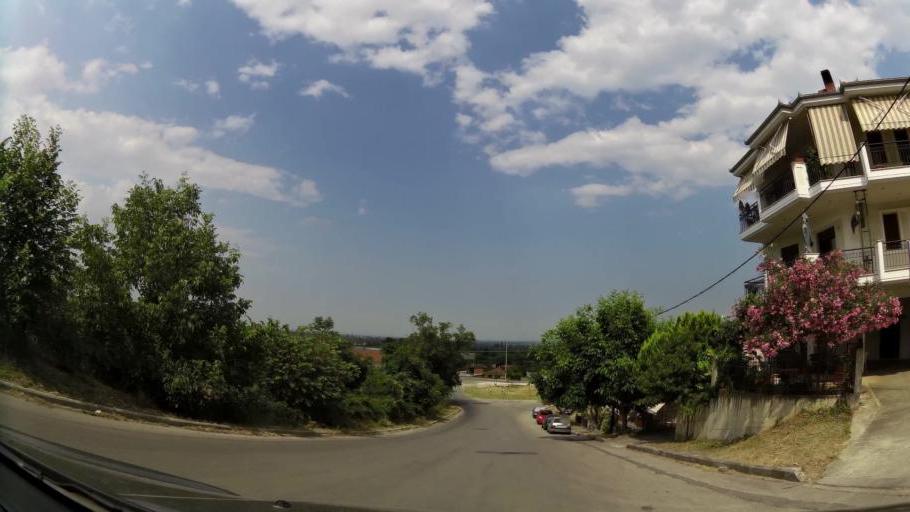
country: GR
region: Central Macedonia
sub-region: Nomos Imathias
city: Veroia
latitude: 40.5135
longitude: 22.2104
